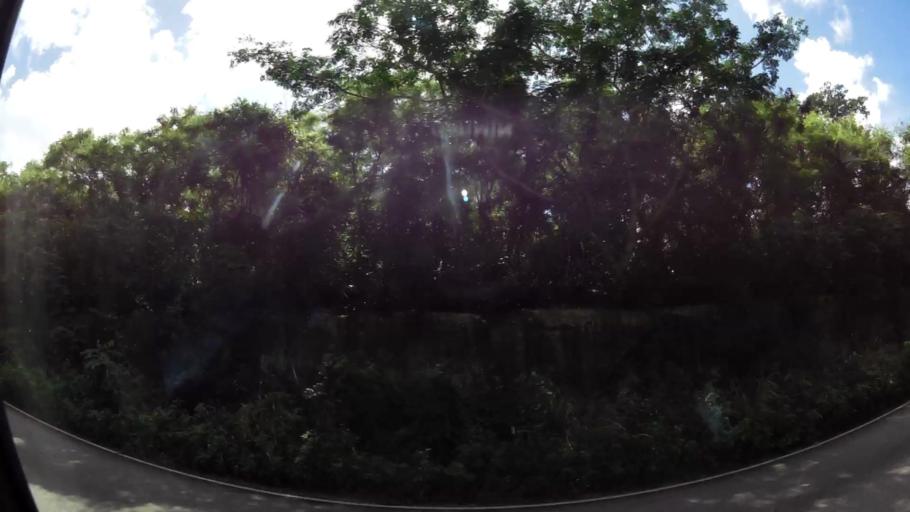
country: BB
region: Saint James
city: Holetown
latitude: 13.1929
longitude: -59.6299
